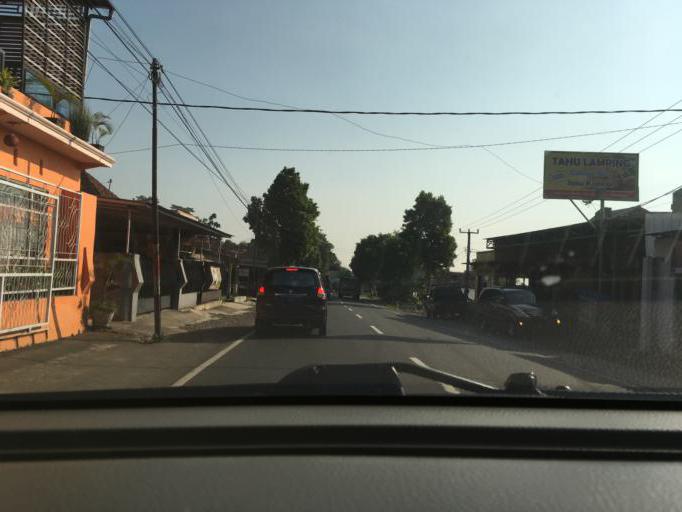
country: ID
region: West Java
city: Kuningan
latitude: -6.9041
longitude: 108.4903
